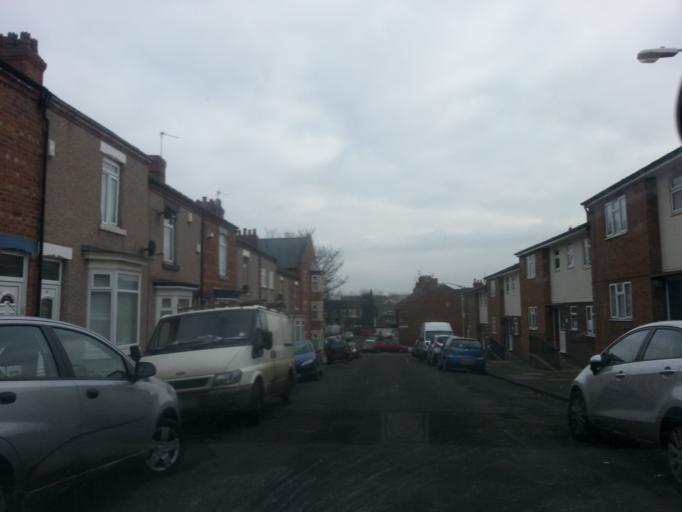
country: GB
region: England
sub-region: Darlington
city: Darlington
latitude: 54.5321
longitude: -1.5550
